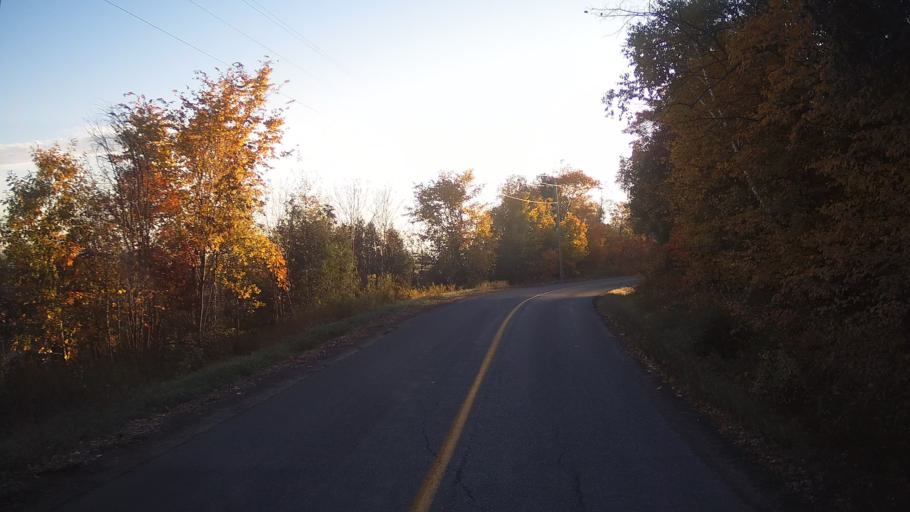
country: CA
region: Ontario
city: Arnprior
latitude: 45.3473
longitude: -76.3402
